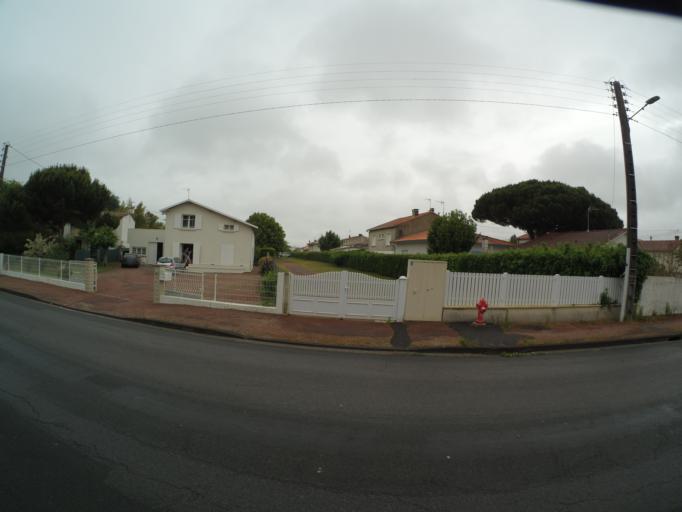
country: FR
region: Poitou-Charentes
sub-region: Departement de la Charente-Maritime
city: Saint-Georges-de-Didonne
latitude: 45.6103
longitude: -0.9962
